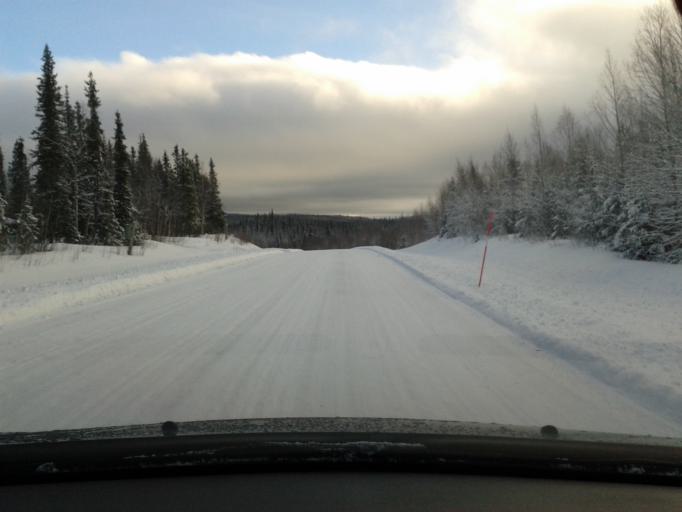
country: SE
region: Vaesterbotten
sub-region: Vilhelmina Kommun
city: Sjoberg
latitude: 65.2578
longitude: 15.6862
